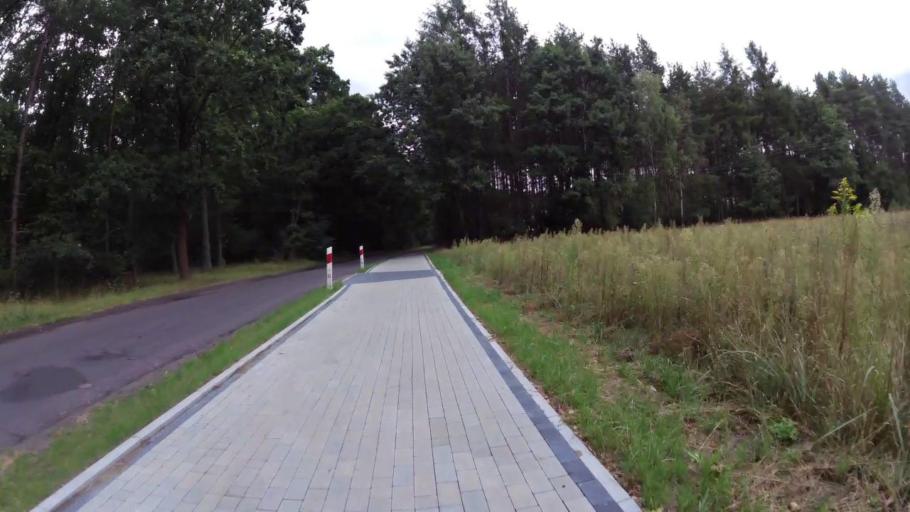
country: PL
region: West Pomeranian Voivodeship
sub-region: Powiat mysliborski
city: Debno
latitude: 52.7649
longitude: 14.6943
